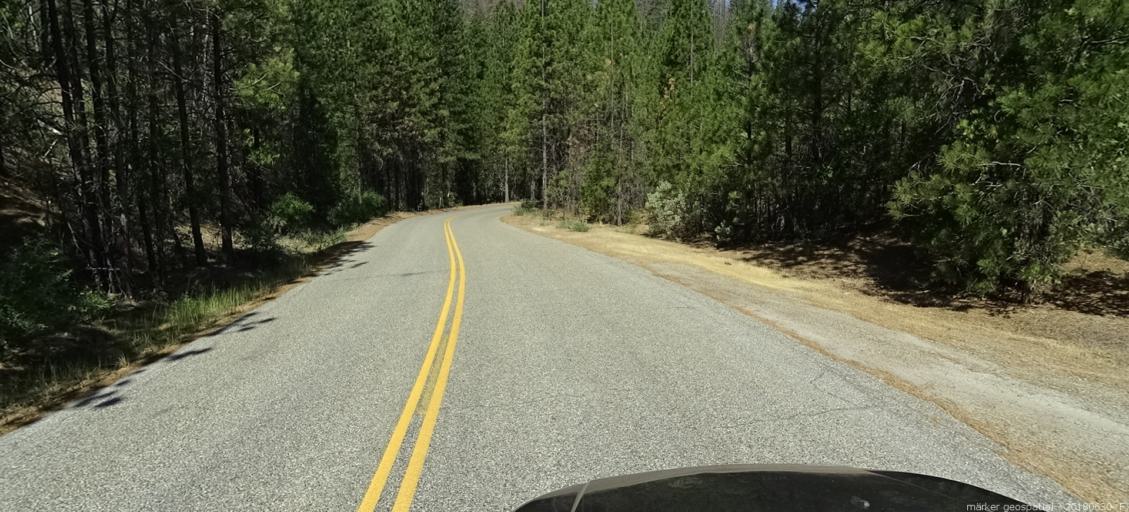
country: US
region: California
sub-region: Madera County
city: Oakhurst
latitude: 37.3659
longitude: -119.3922
